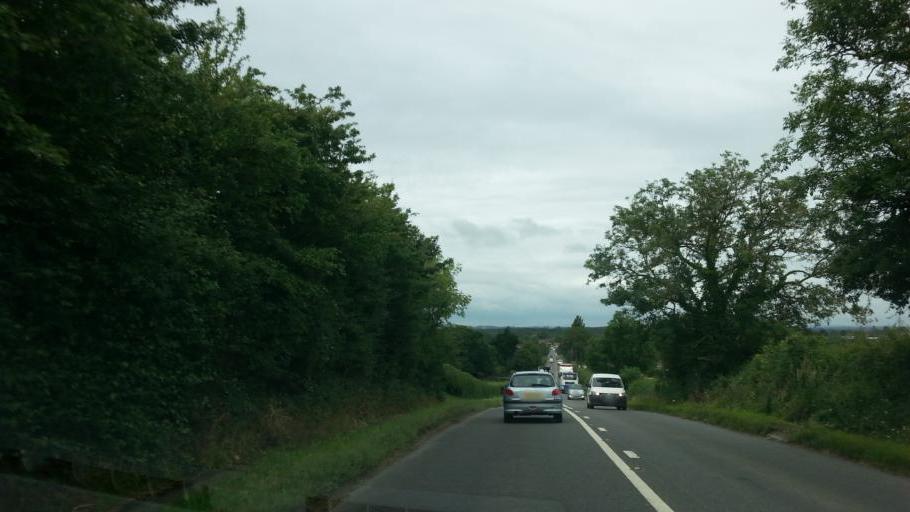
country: GB
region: England
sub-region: Wiltshire
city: North Bradley
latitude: 51.2989
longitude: -2.1809
